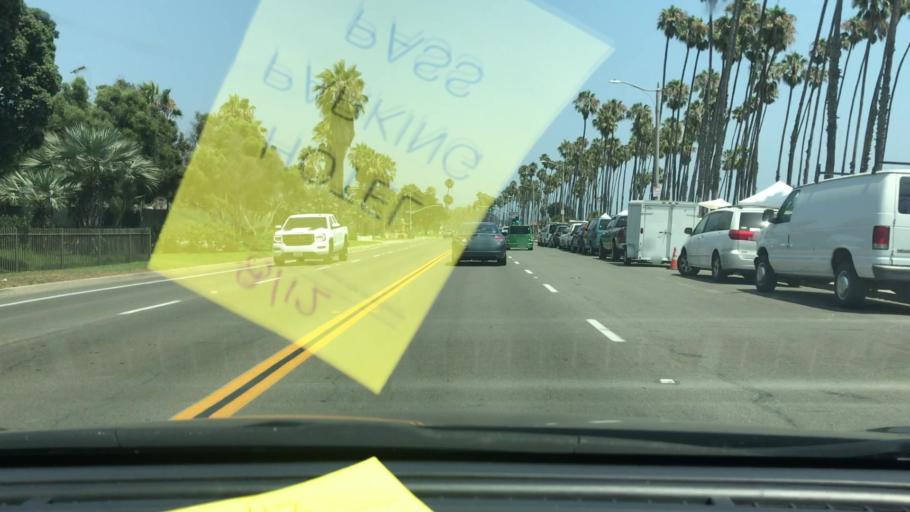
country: US
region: California
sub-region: Santa Barbara County
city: Santa Barbara
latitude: 34.4151
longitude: -119.6824
